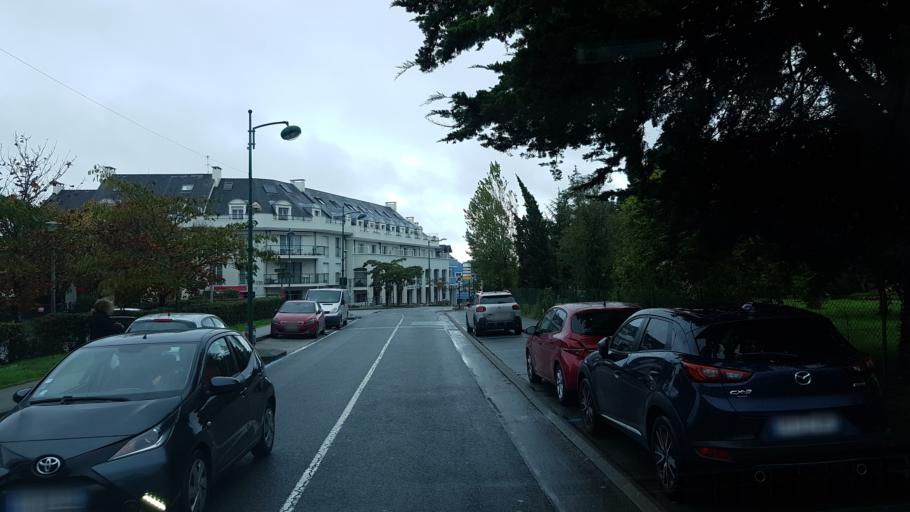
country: FR
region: Brittany
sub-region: Departement du Morbihan
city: Sarzeau
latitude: 47.5262
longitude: -2.7700
